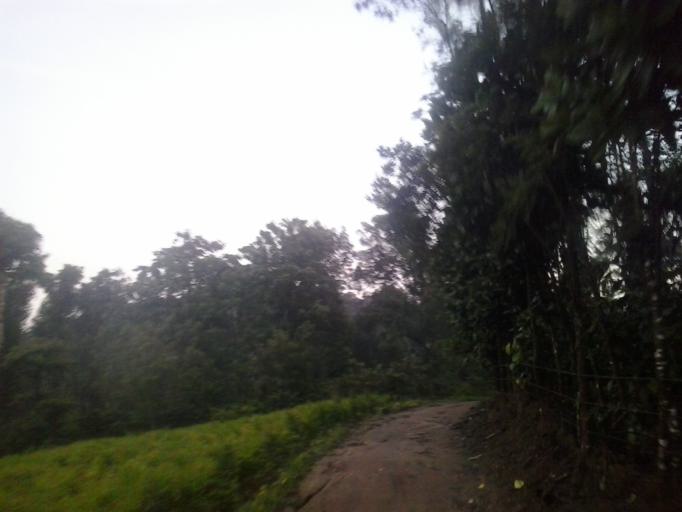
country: IN
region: Karnataka
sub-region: Chikmagalur
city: Mudigere
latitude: 13.0120
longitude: 75.6706
